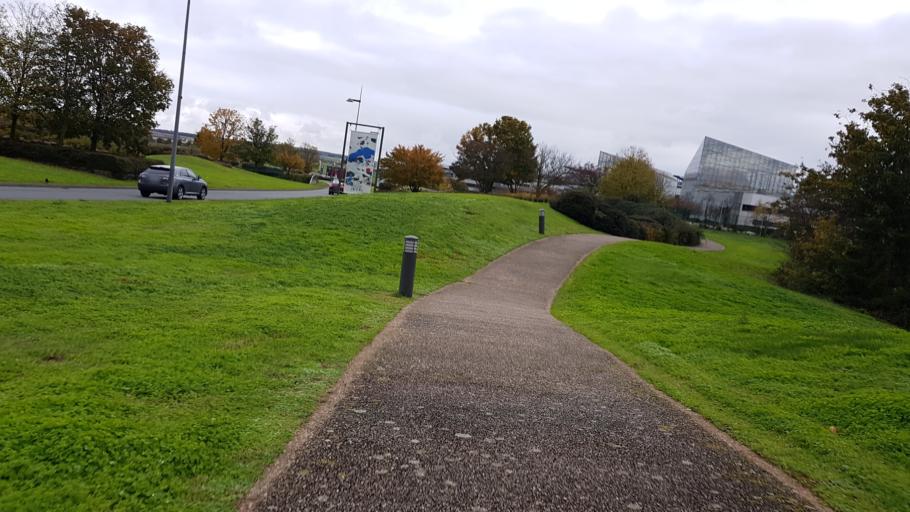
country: FR
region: Poitou-Charentes
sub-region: Departement de la Vienne
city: Chasseneuil-du-Poitou
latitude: 46.6621
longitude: 0.3624
